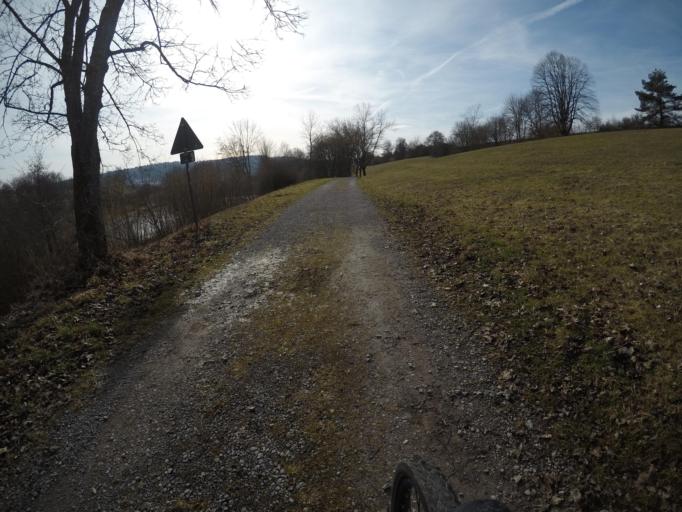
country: DE
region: Baden-Wuerttemberg
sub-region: Karlsruhe Region
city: Wildberg
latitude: 48.6570
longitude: 8.7731
